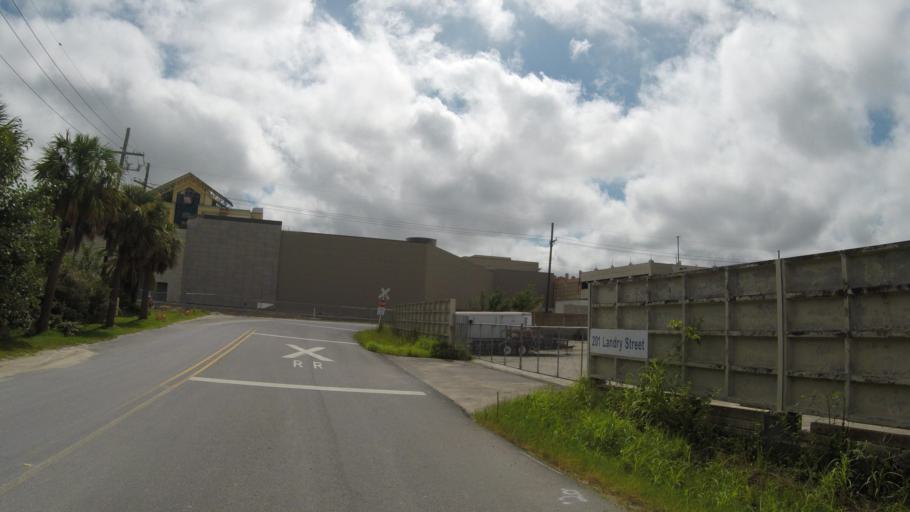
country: US
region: Louisiana
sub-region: Calcasieu Parish
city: Westlake
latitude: 30.2347
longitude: -93.2502
